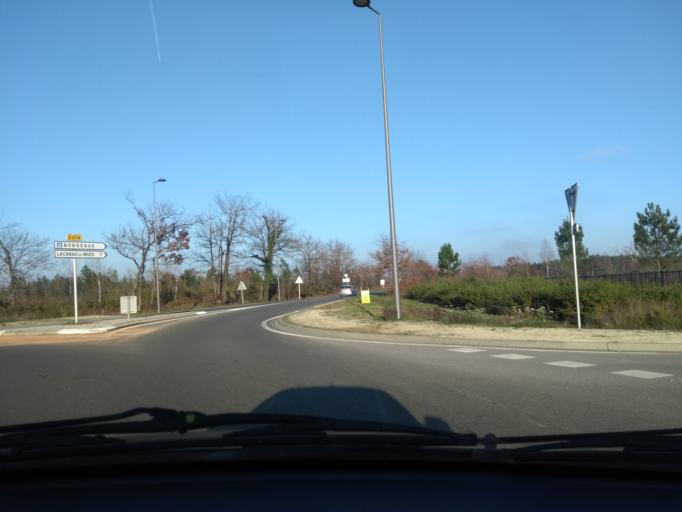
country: FR
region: Aquitaine
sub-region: Departement de la Gironde
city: Mios
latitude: 44.6176
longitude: -0.9169
